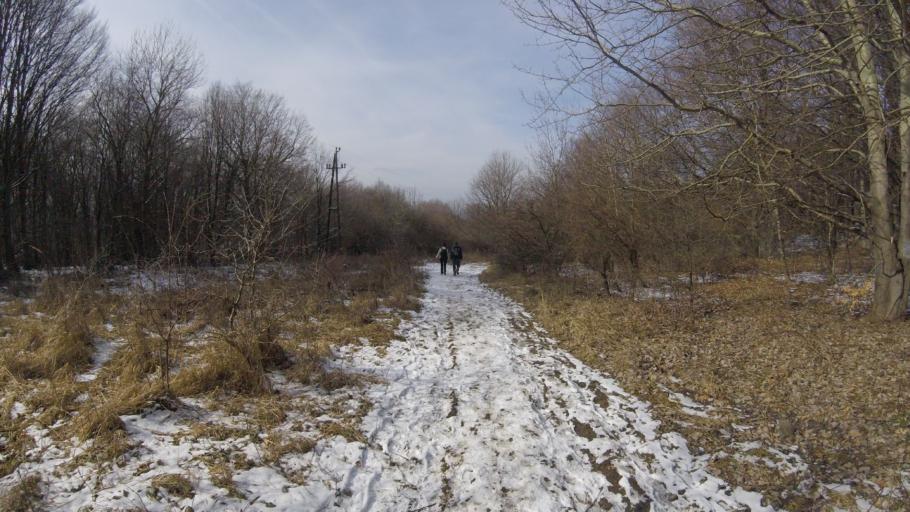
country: HU
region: Nograd
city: Batonyterenye
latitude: 47.9162
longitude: 19.8932
